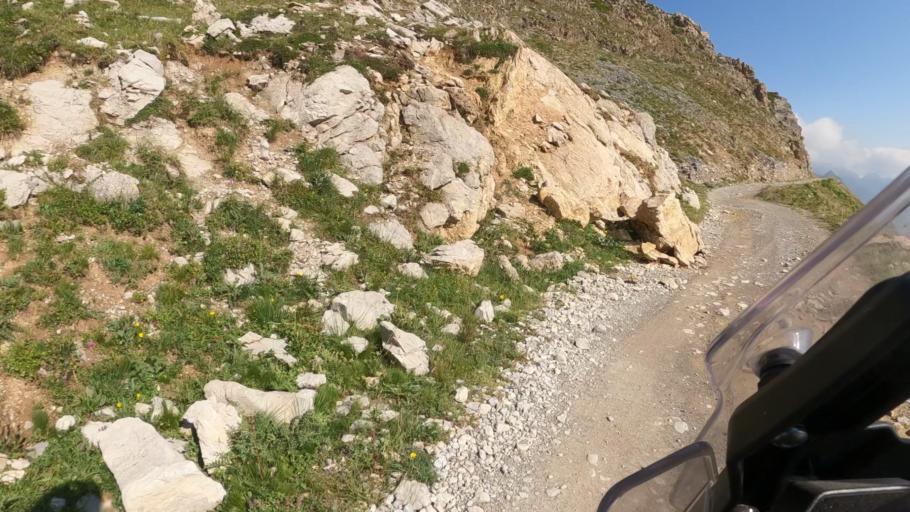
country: IT
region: Piedmont
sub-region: Provincia di Cuneo
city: Pietraporzio
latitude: 44.3889
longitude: 7.0279
